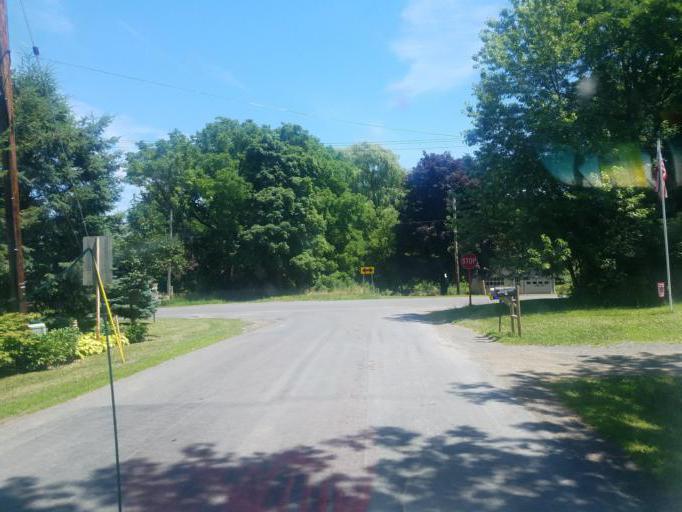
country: US
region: New York
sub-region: Yates County
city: Penn Yan
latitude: 42.6340
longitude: -77.0000
